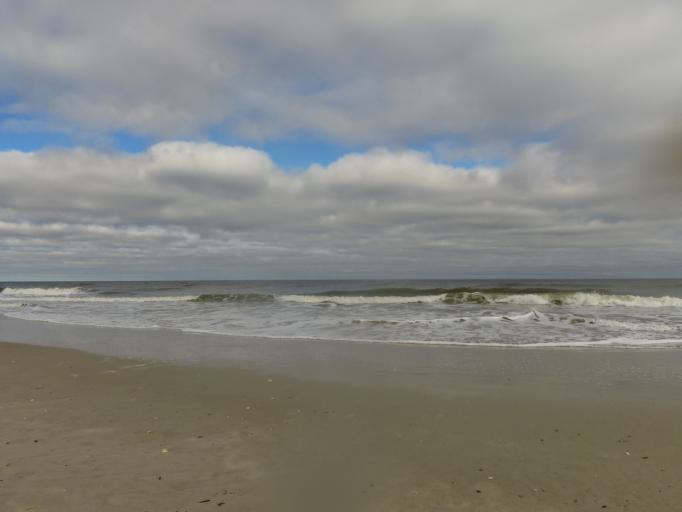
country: US
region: Florida
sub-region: Nassau County
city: Fernandina Beach
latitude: 30.5536
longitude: -81.4418
